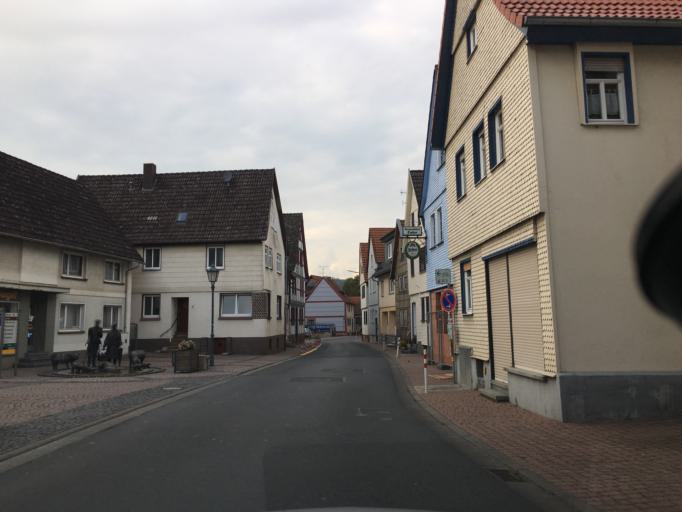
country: DE
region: Hesse
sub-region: Regierungsbezirk Darmstadt
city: Steinau an der Strasse
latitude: 50.3137
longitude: 9.4648
